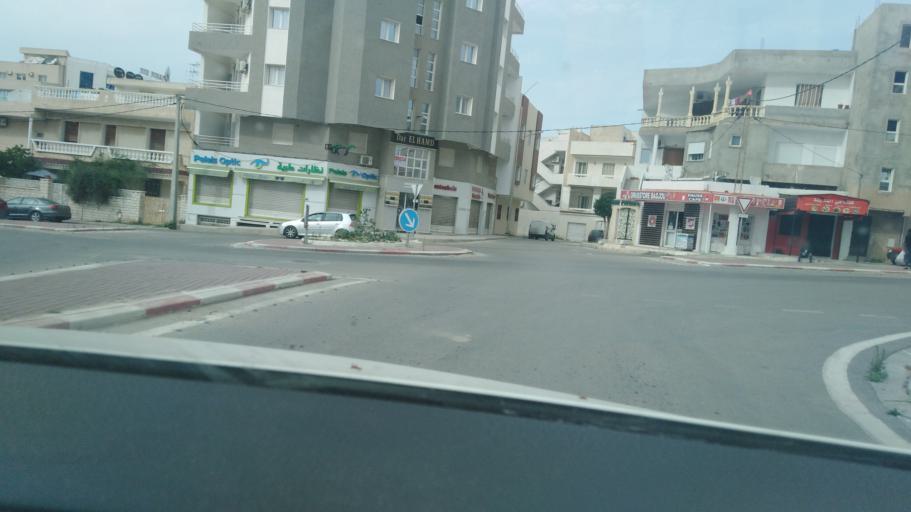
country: TN
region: Susah
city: Sousse
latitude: 35.8266
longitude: 10.6330
